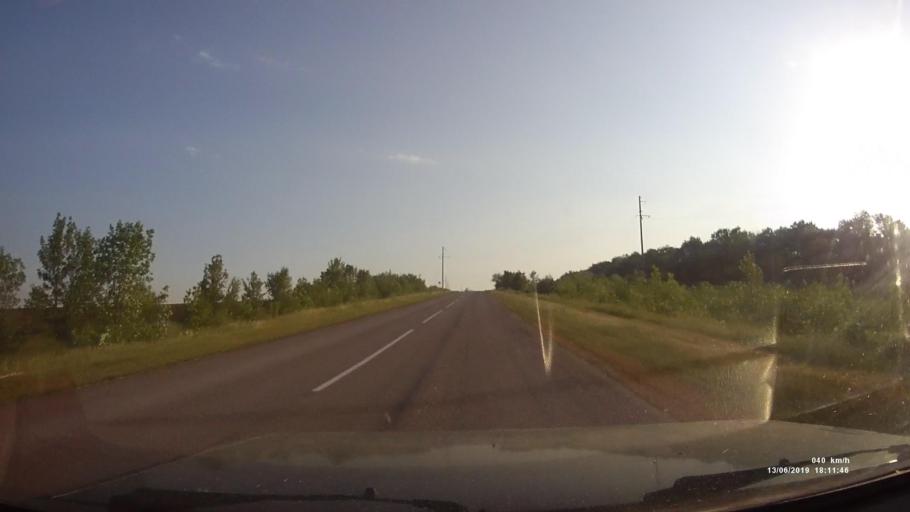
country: RU
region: Rostov
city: Kazanskaya
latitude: 49.9493
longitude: 41.4175
